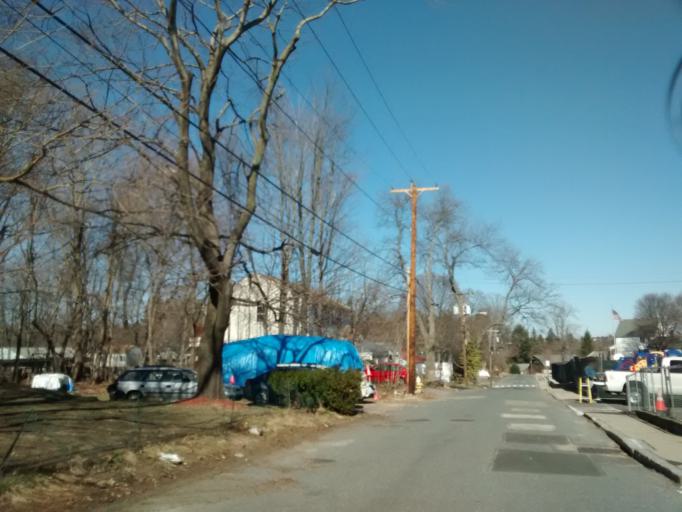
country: US
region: Massachusetts
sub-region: Worcester County
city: Worcester
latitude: 42.2952
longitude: -71.8230
